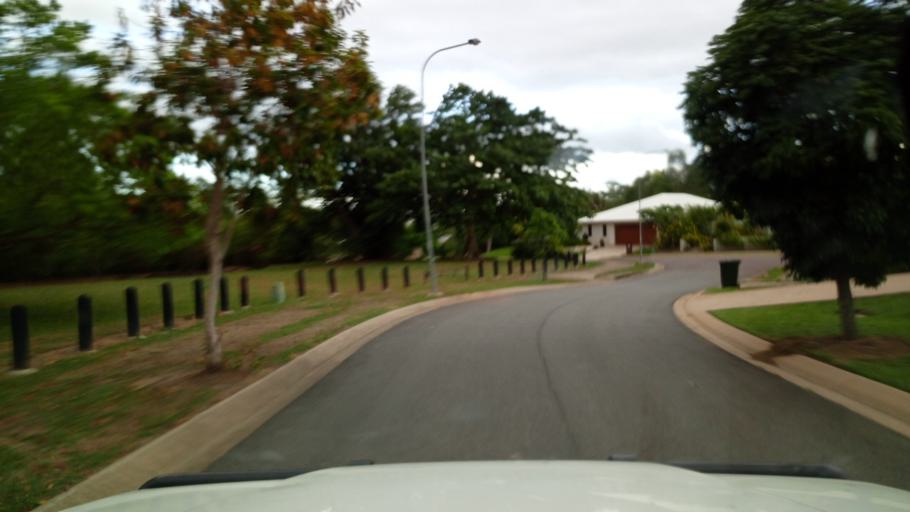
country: AU
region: Queensland
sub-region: Cairns
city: Redlynch
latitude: -16.8431
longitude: 145.6880
